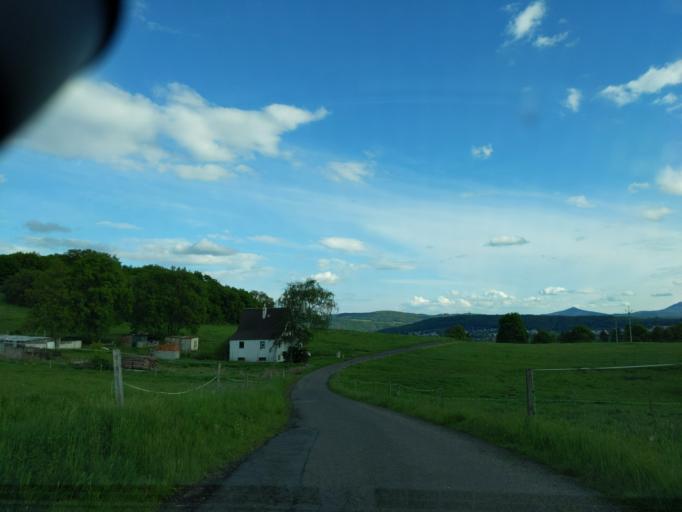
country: CZ
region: Ustecky
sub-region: Okres Usti nad Labem
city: Usti nad Labem
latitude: 50.7109
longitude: 14.0013
